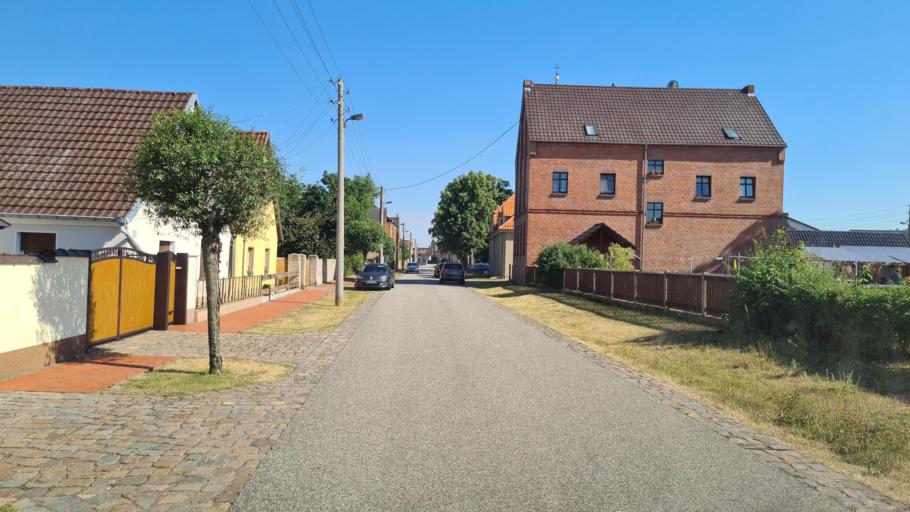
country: DE
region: Saxony-Anhalt
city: Annaburg
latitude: 51.6977
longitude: 12.9947
